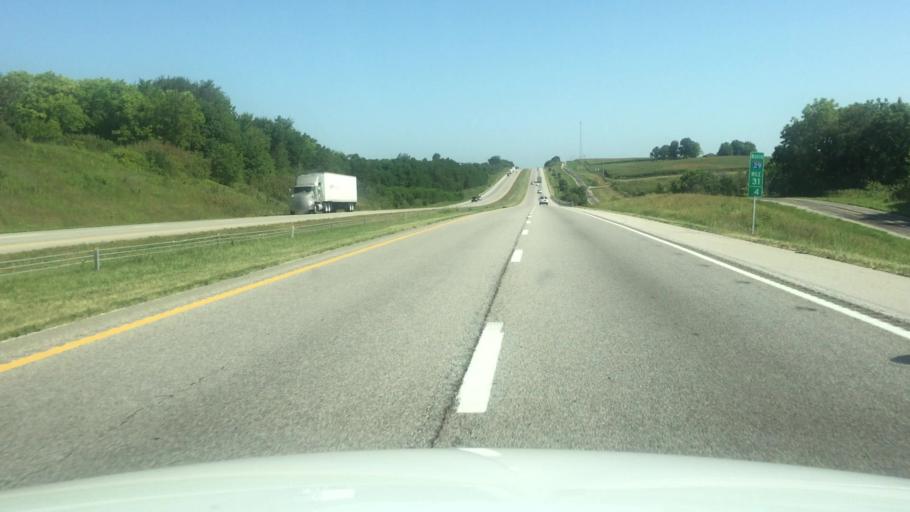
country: US
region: Missouri
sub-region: Platte County
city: Platte City
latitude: 39.5371
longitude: -94.7873
